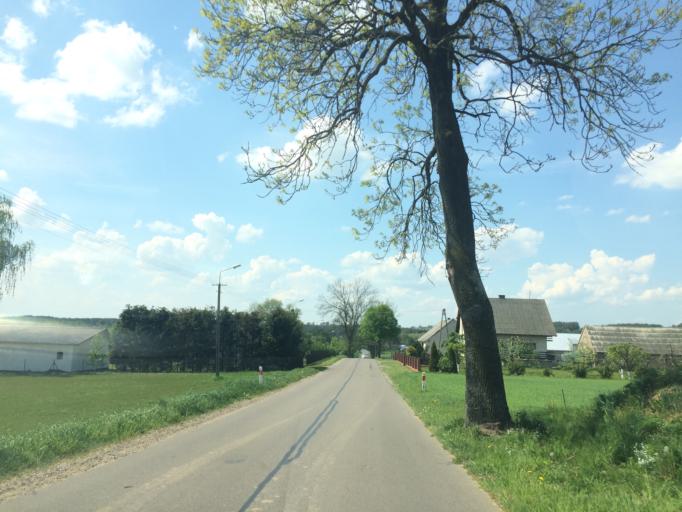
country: PL
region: Warmian-Masurian Voivodeship
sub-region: Powiat ilawski
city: Lubawa
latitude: 53.4334
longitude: 19.7002
